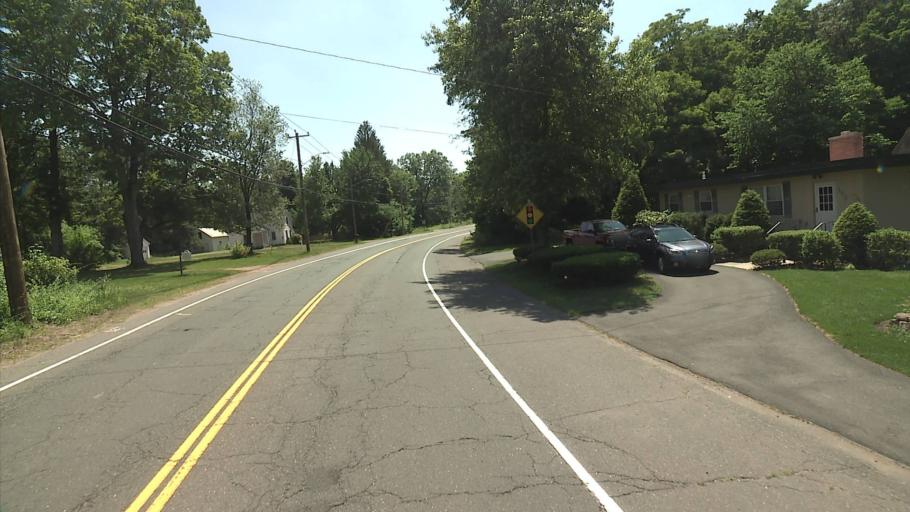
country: US
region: Connecticut
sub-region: Hartford County
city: South Windsor
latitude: 41.8150
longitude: -72.5905
